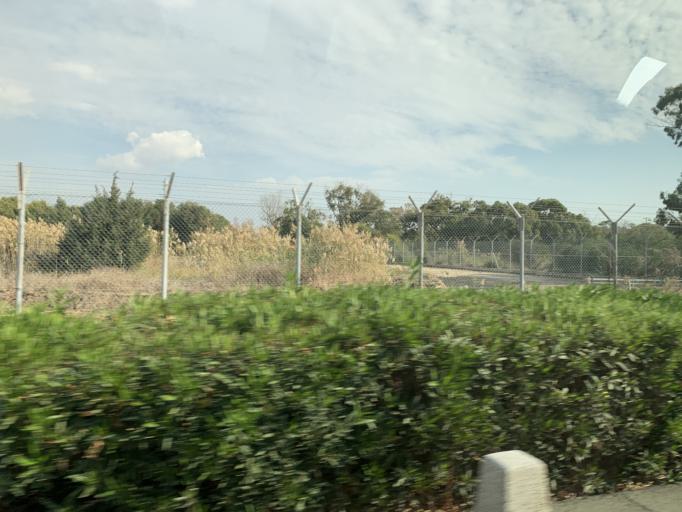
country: CY
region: Pafos
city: Paphos
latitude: 34.7115
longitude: 32.4909
